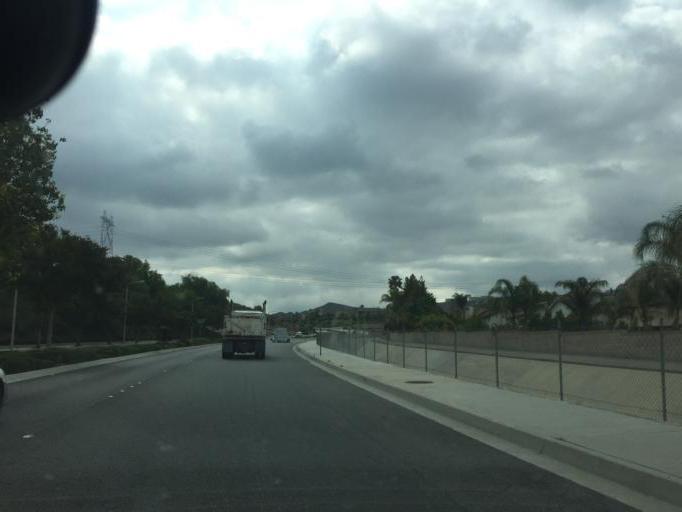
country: US
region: California
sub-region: Los Angeles County
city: Santa Clarita
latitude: 34.4483
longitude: -118.4920
